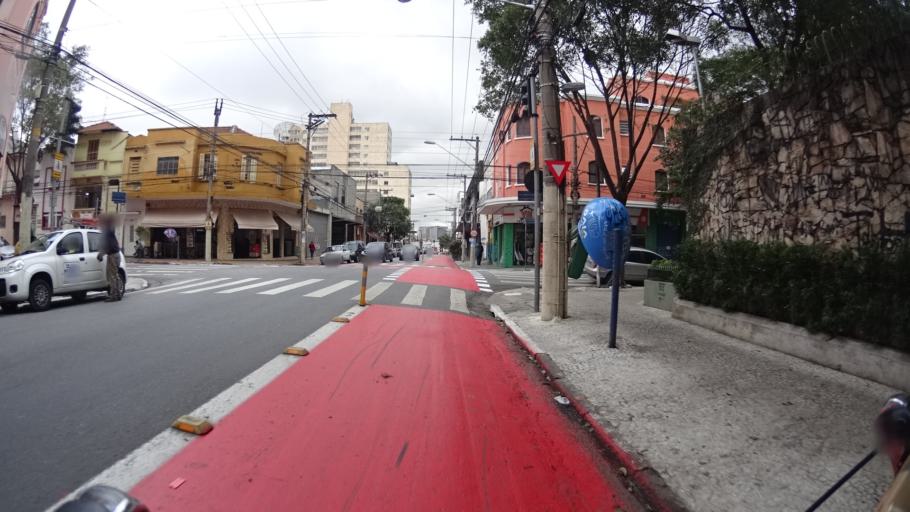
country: BR
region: Sao Paulo
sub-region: Sao Paulo
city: Sao Paulo
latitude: -23.5323
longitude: -46.6535
